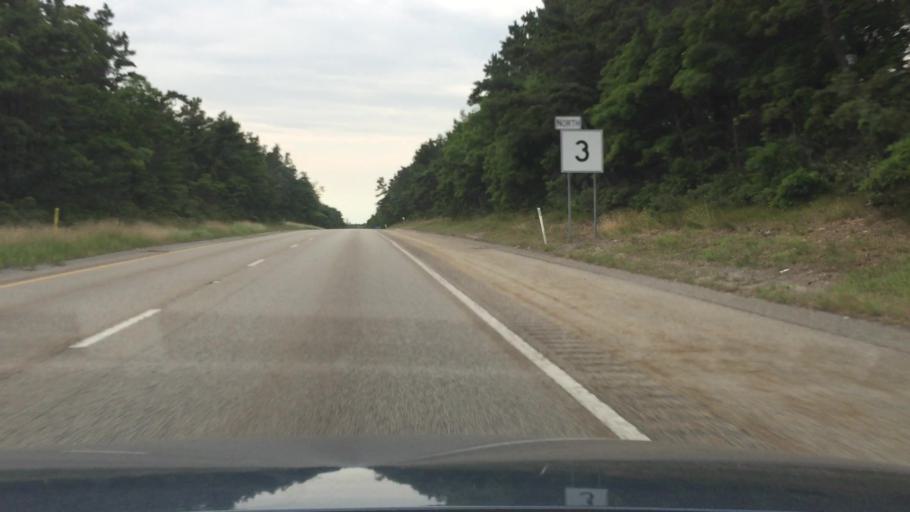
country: US
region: Massachusetts
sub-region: Plymouth County
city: White Island Shores
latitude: 41.8419
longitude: -70.5707
